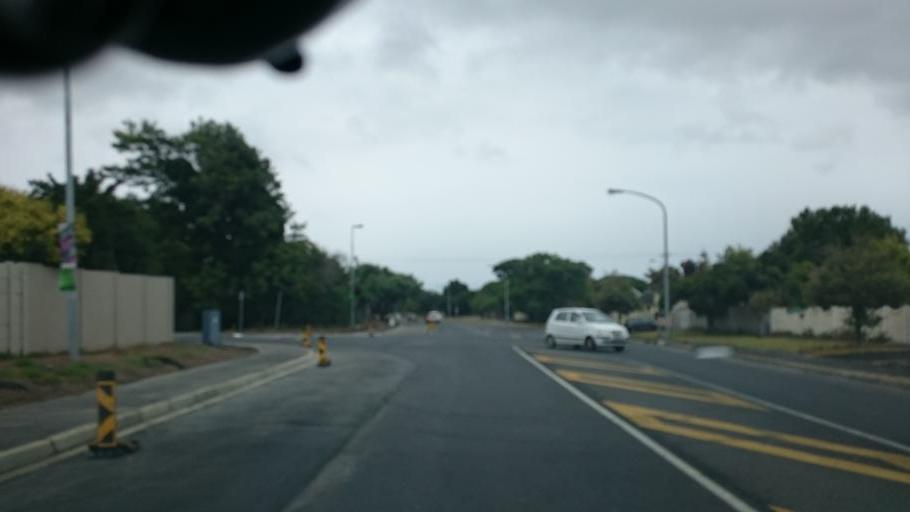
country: ZA
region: Western Cape
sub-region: City of Cape Town
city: Bergvliet
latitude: -34.0317
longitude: 18.4540
